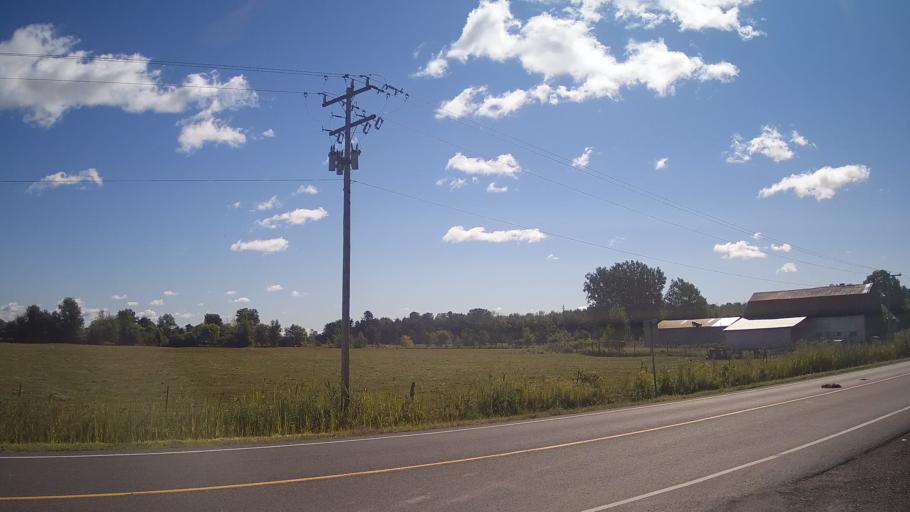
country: CA
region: Ontario
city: Prescott
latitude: 44.9032
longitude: -75.4003
